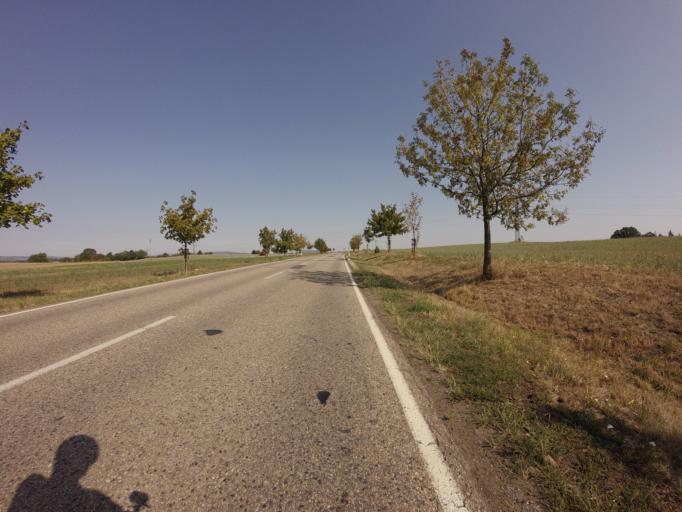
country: CZ
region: Central Bohemia
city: Porici nad Sazavou
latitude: 49.8057
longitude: 14.6504
